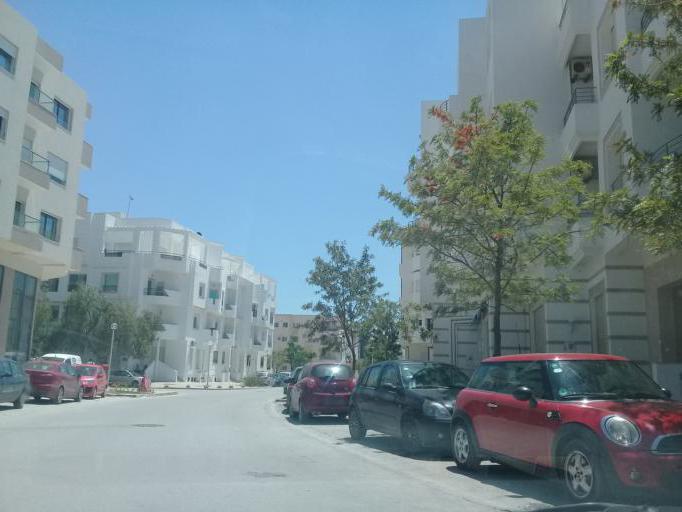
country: TN
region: Tunis
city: La Goulette
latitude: 36.8470
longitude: 10.2747
